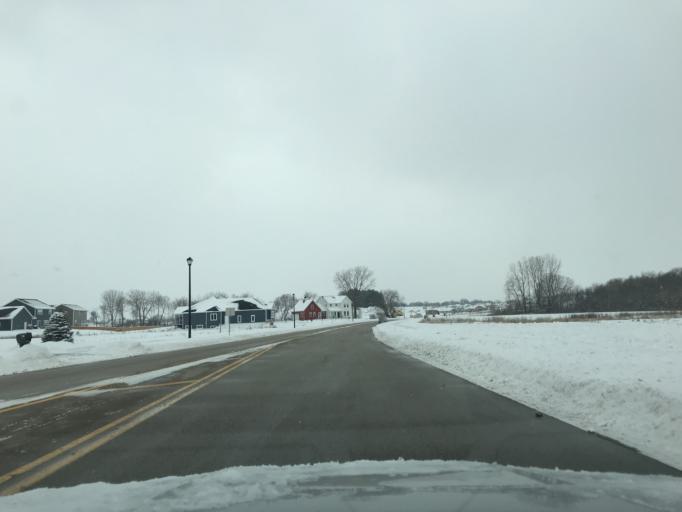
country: US
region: Wisconsin
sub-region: Dane County
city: Sun Prairie
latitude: 43.1761
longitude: -89.2717
